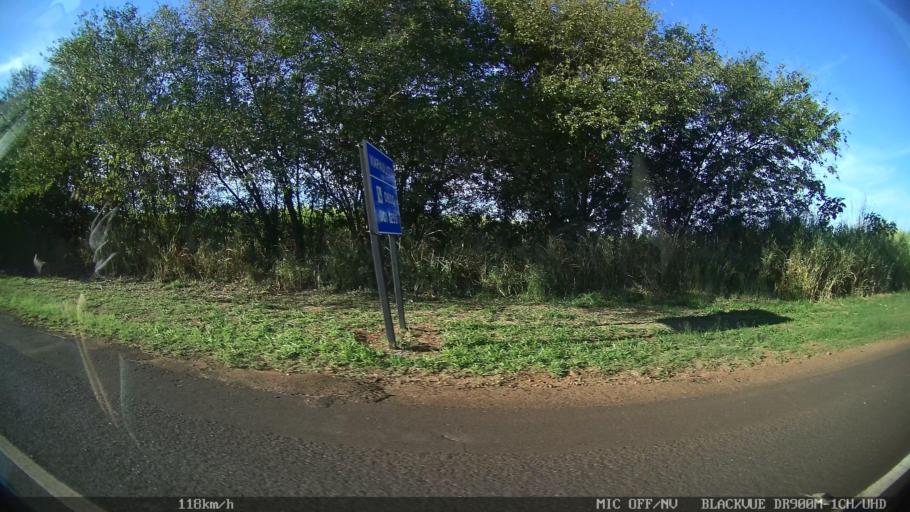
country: BR
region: Sao Paulo
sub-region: Americo Brasiliense
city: Americo Brasiliense
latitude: -21.7662
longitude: -48.1103
